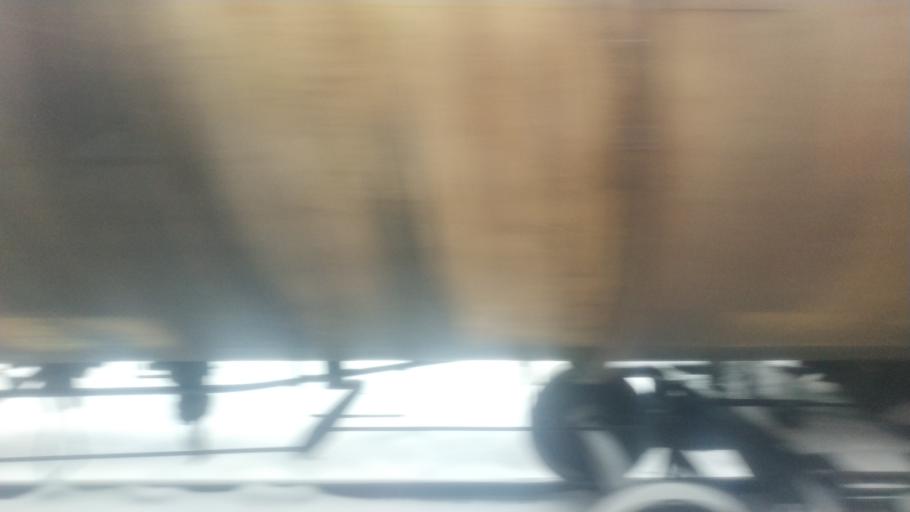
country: RU
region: Udmurtiya
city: Kama
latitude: 56.2954
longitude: 54.1146
